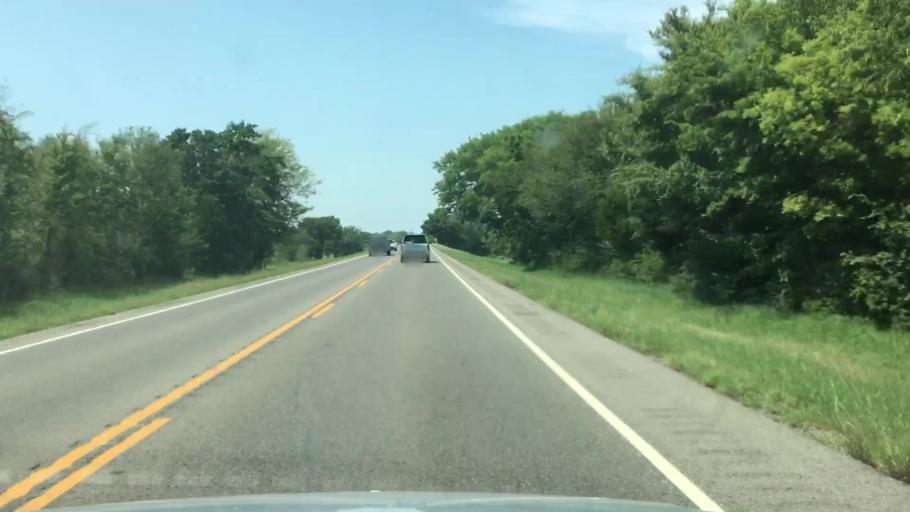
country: US
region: Oklahoma
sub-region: Wagoner County
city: Wagoner
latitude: 35.9371
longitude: -95.3223
